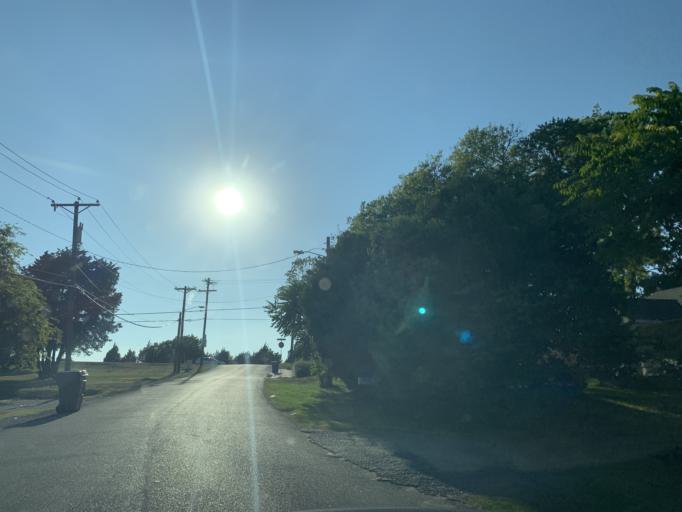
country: US
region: Texas
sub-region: Dallas County
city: Hutchins
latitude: 32.6695
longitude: -96.7819
